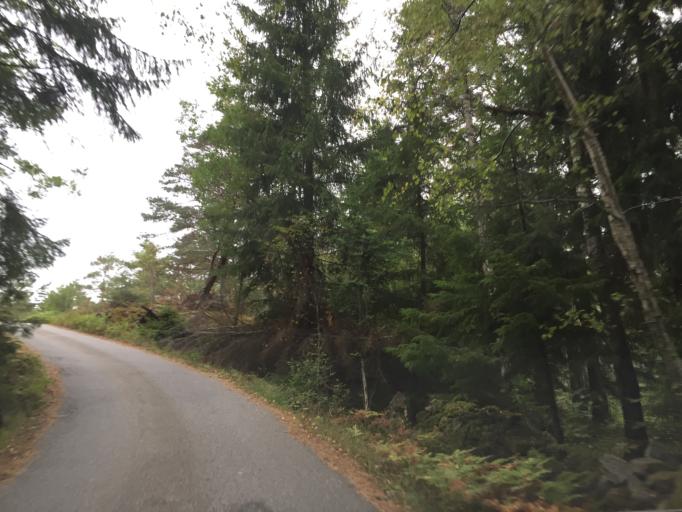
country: NO
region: Ostfold
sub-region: Hvaler
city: Skjaerhalden
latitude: 59.0790
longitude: 11.0050
